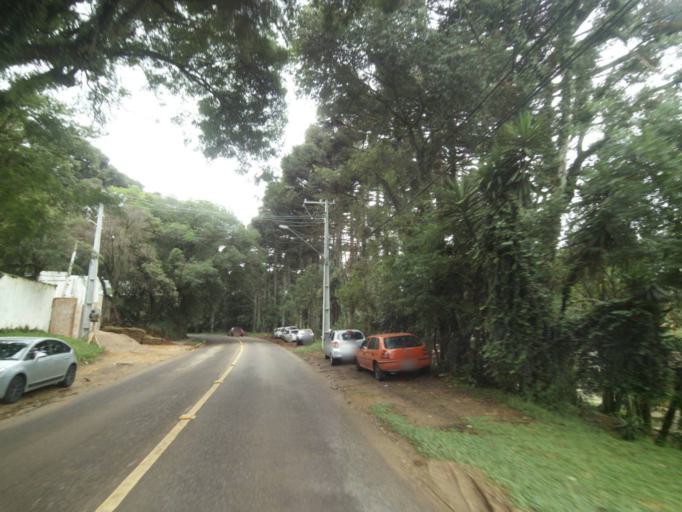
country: BR
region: Parana
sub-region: Curitiba
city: Curitiba
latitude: -25.4493
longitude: -49.3308
